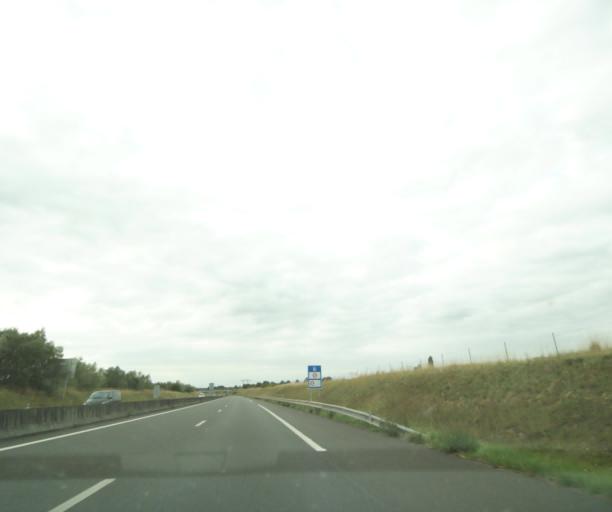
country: FR
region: Centre
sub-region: Departement d'Indre-et-Loire
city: Parcay-Meslay
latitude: 47.4763
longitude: 0.7551
